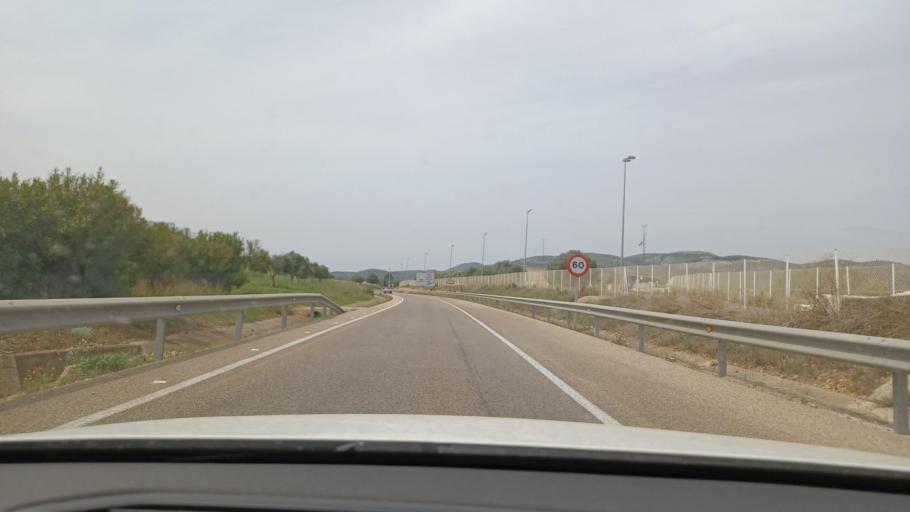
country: ES
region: Valencia
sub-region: Provincia de Castello
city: Peniscola
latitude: 40.3960
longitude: 0.3607
